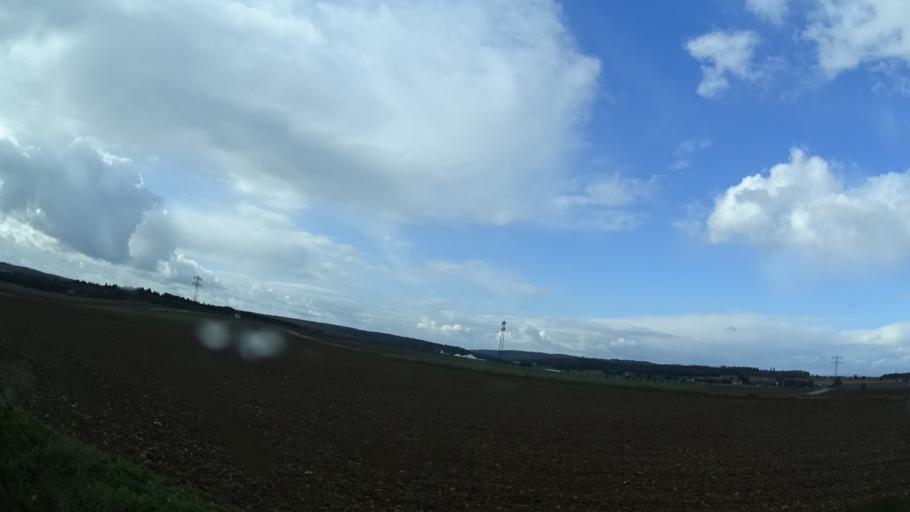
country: DE
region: Baden-Wuerttemberg
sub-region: Karlsruhe Region
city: Hardheim
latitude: 49.6402
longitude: 9.4905
